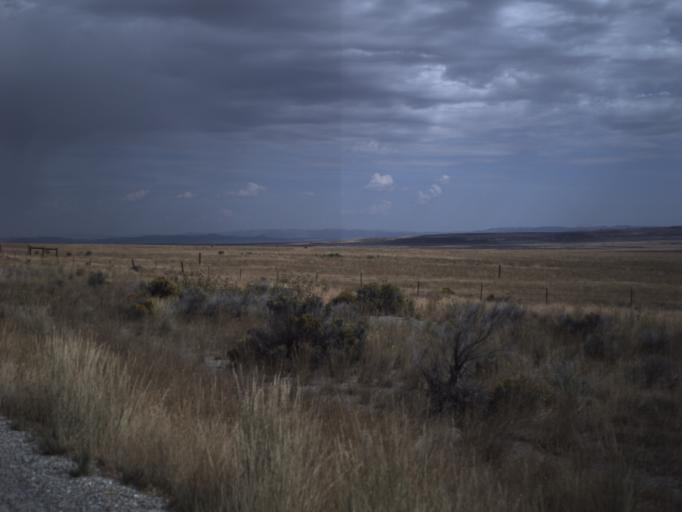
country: US
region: Idaho
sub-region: Minidoka County
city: Rupert
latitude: 41.8470
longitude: -113.1367
